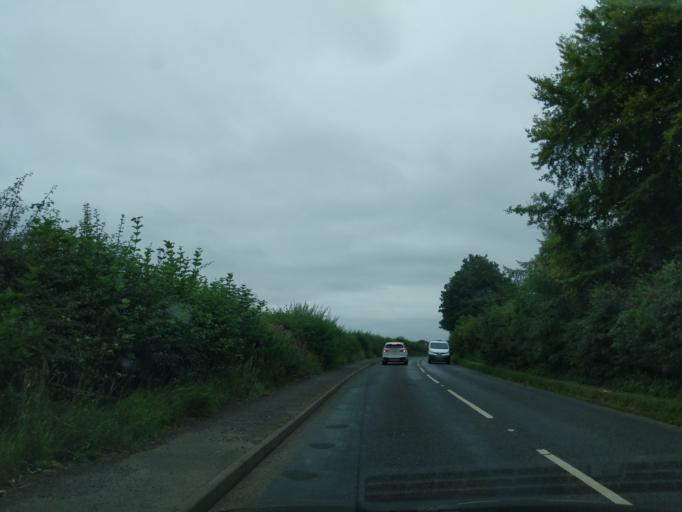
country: GB
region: Scotland
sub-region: East Lothian
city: Pencaitland
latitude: 55.9095
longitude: -2.9054
